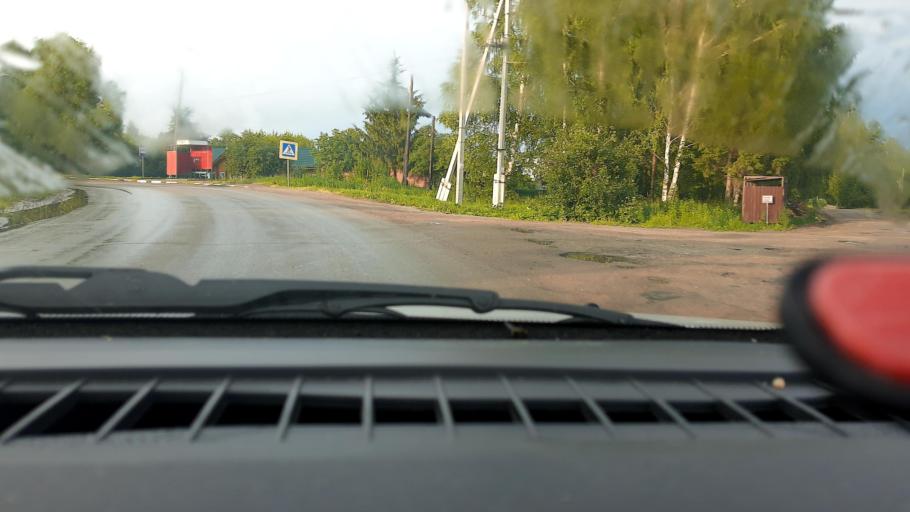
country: RU
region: Nizjnij Novgorod
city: Lukoyanov
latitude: 55.0377
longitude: 44.4949
